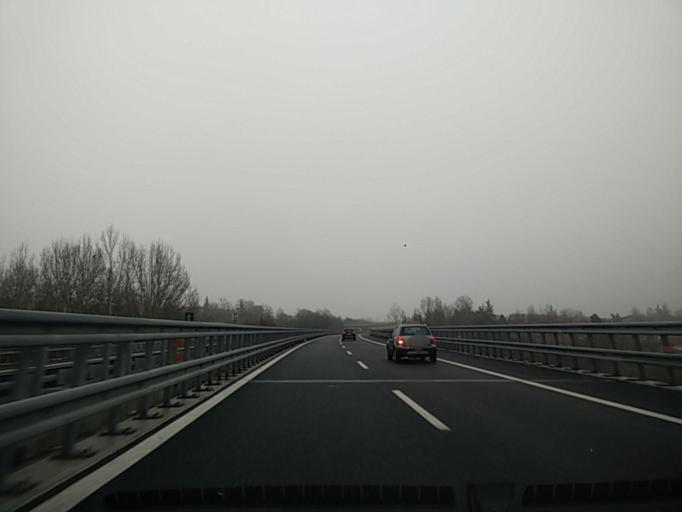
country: IT
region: Piedmont
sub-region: Provincia di Asti
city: Asti
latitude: 44.9176
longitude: 8.1963
